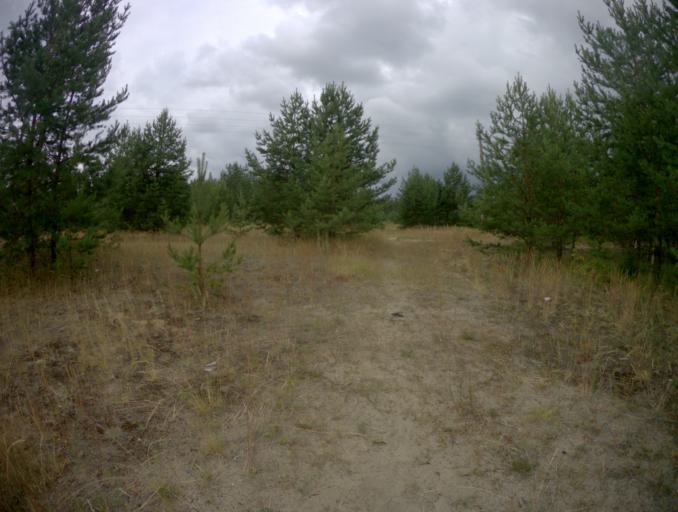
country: RU
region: Nizjnij Novgorod
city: Frolishchi
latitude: 56.4128
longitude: 42.6343
